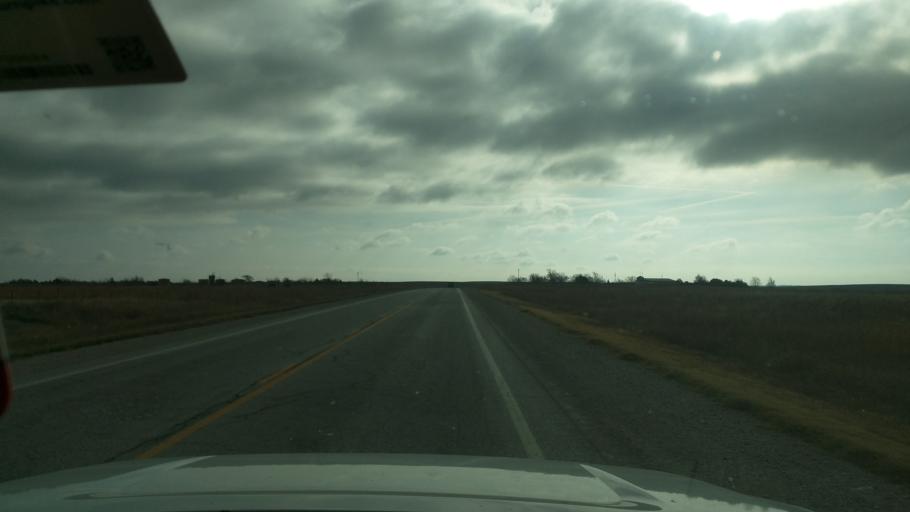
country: US
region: Kansas
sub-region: Chautauqua County
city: Sedan
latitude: 37.1050
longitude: -96.2439
